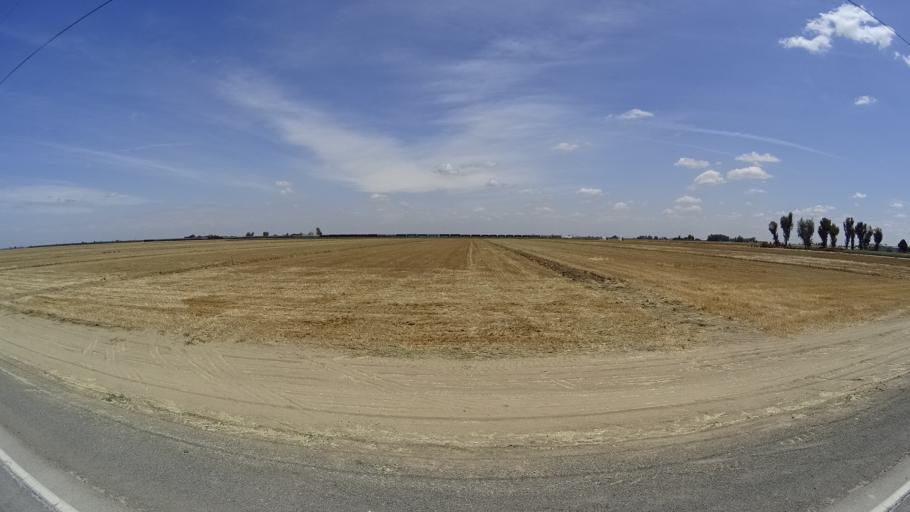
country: US
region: California
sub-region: Kings County
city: Home Garden
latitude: 36.2342
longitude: -119.6548
